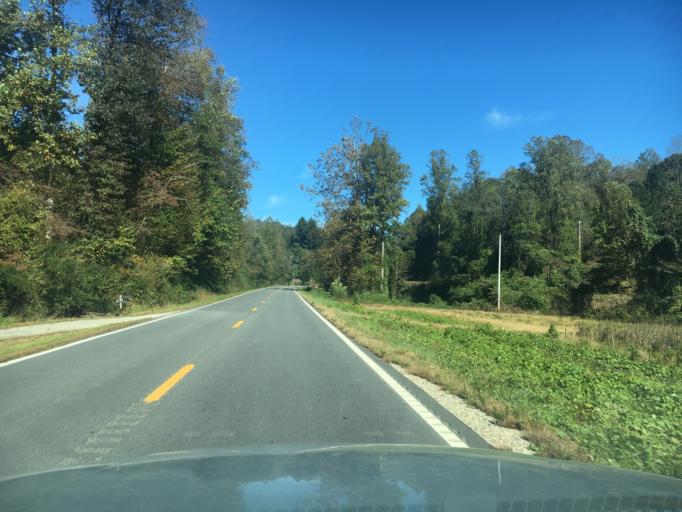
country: US
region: North Carolina
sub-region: Burke County
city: Glen Alpine
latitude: 35.5539
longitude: -81.8547
